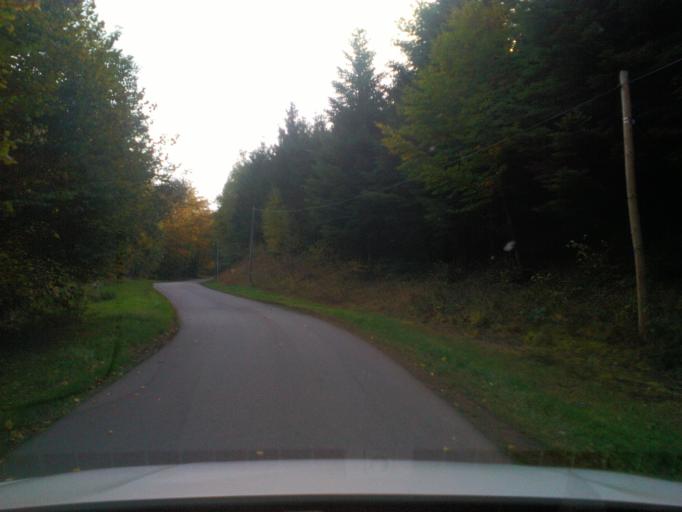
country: FR
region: Lorraine
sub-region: Departement des Vosges
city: Senones
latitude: 48.3823
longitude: 7.0087
